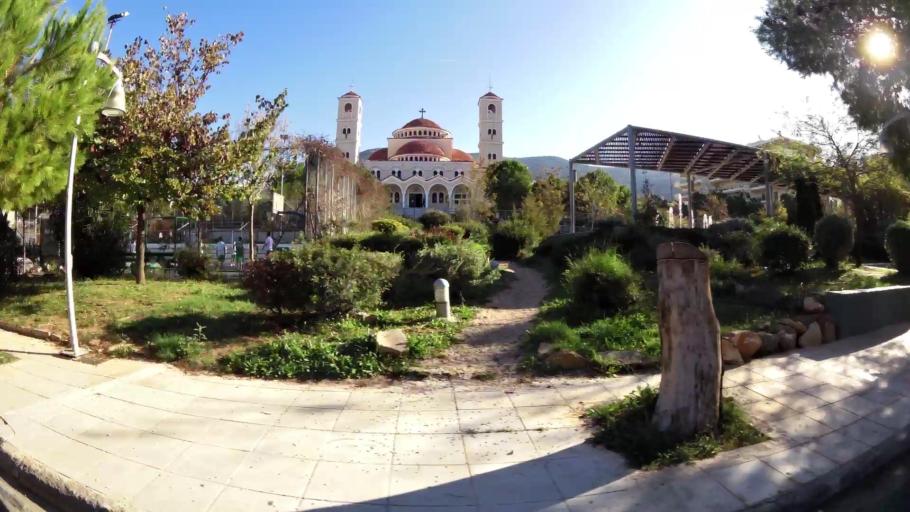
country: GR
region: Attica
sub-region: Nomarchia Athinas
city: Glyfada
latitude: 37.8725
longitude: 23.7655
